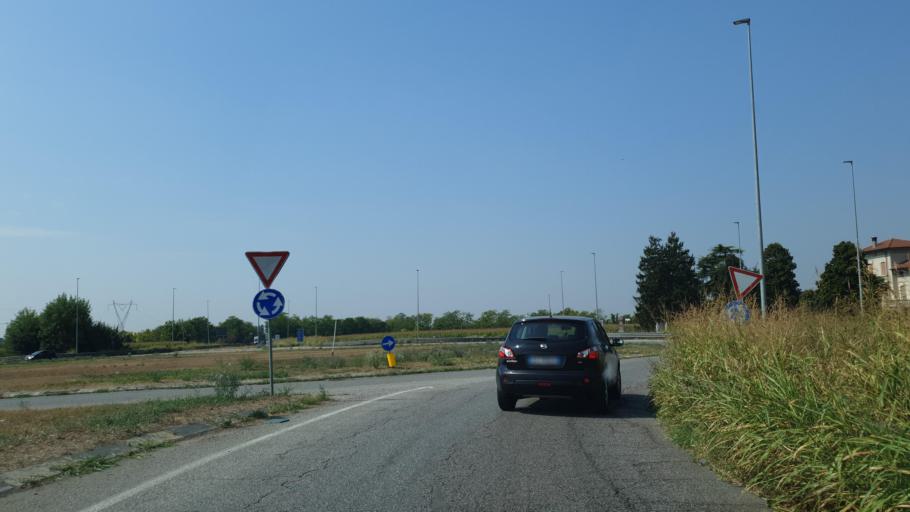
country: IT
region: Lombardy
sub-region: Provincia di Brescia
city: Leno
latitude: 45.3765
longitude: 10.2030
